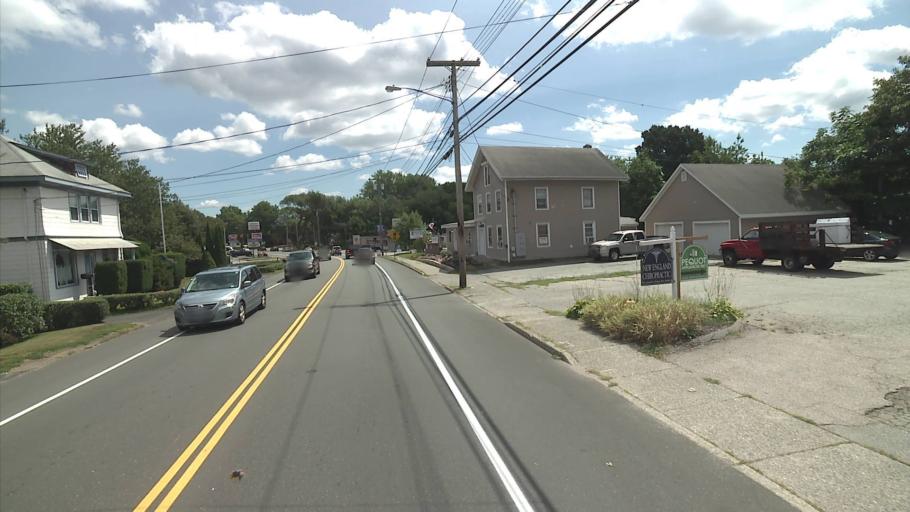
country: US
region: Connecticut
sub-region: New London County
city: Poquonock Bridge
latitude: 41.3461
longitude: -72.0360
